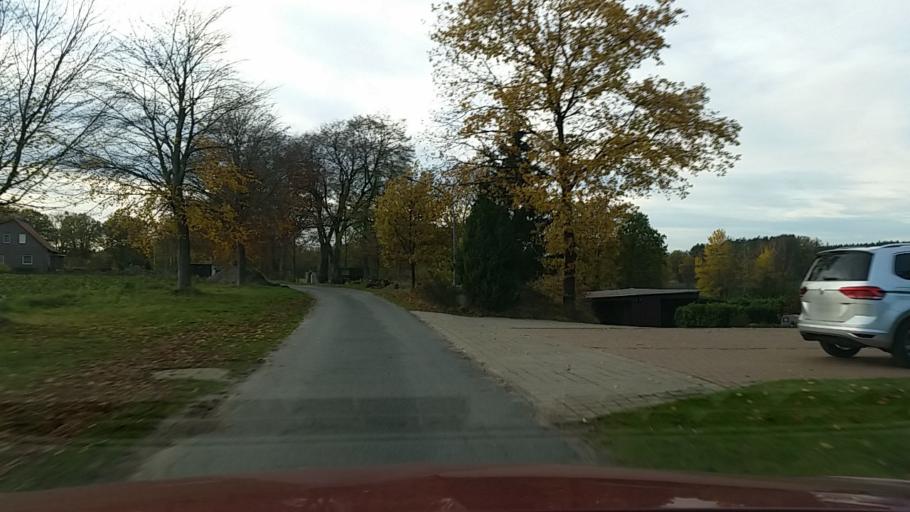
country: DE
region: Lower Saxony
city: Sprakensehl
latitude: 52.8086
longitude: 10.5289
